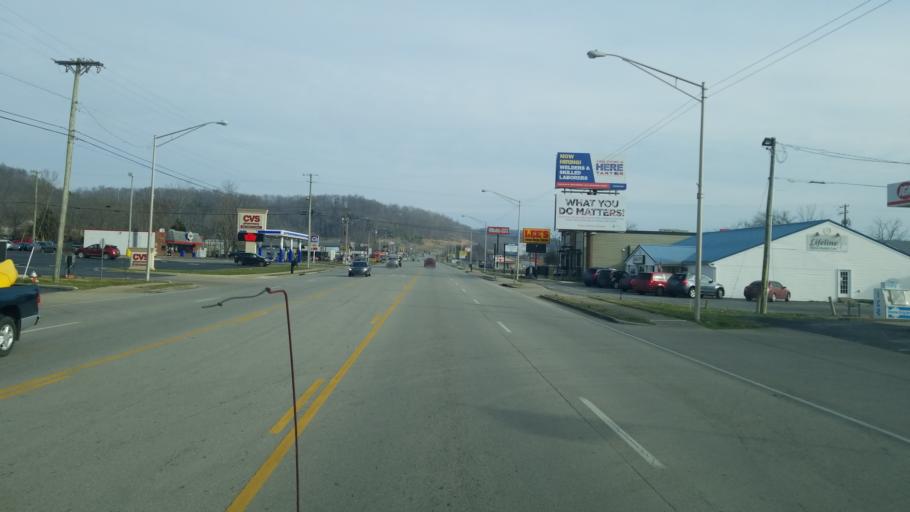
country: US
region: Kentucky
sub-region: Casey County
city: Liberty
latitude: 37.3191
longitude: -84.9285
